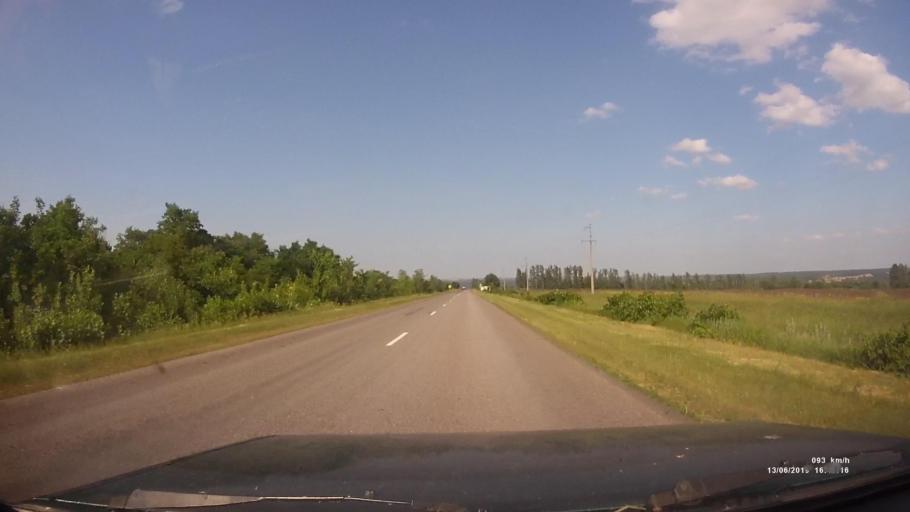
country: RU
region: Rostov
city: Kazanskaya
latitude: 49.9412
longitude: 41.4003
